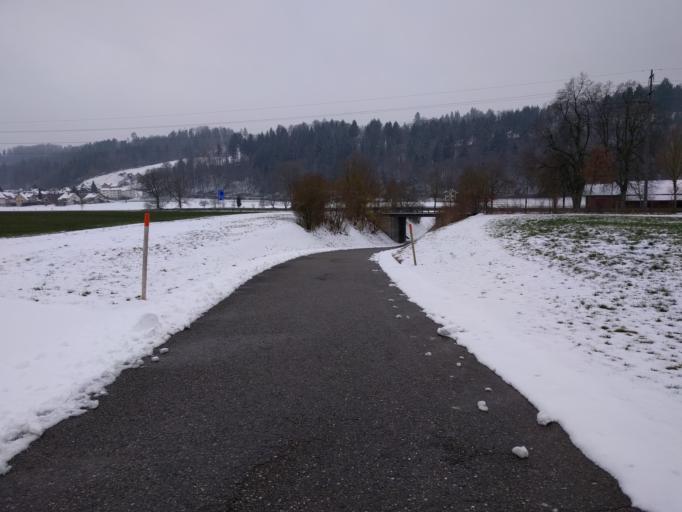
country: CH
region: Aargau
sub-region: Bezirk Kulm
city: Schoftland
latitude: 47.3065
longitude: 8.0455
